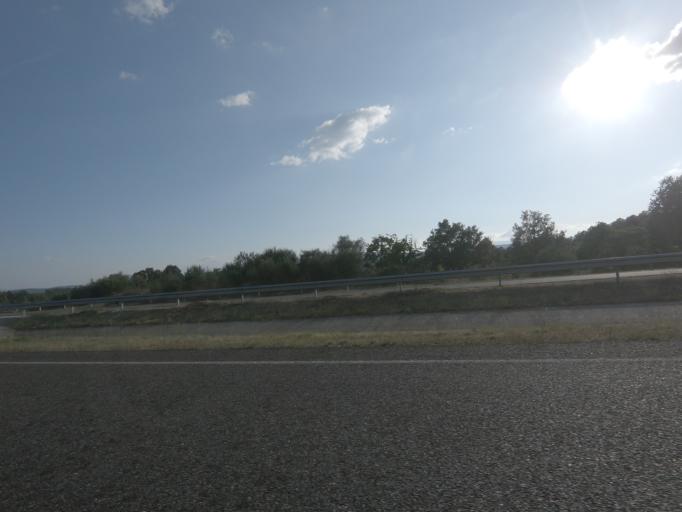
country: ES
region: Galicia
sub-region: Provincia de Ourense
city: Verin
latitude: 41.8978
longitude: -7.4245
